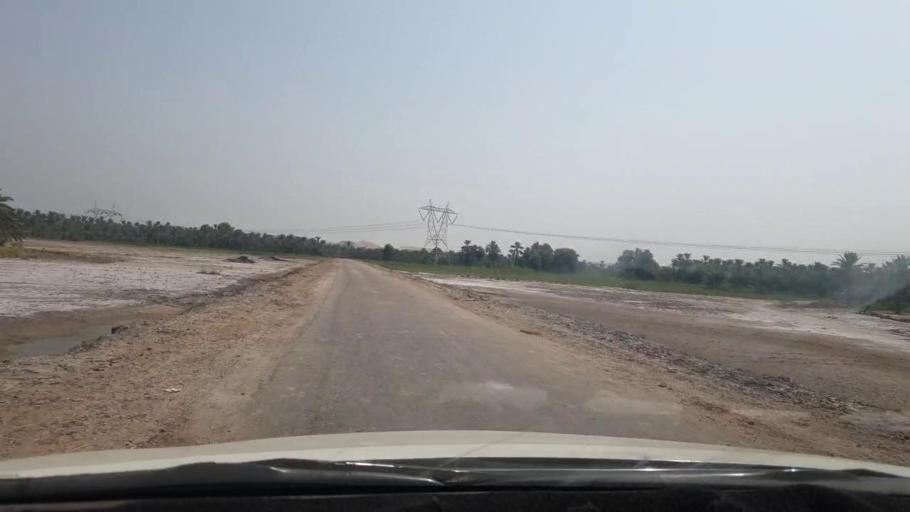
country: PK
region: Sindh
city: Rohri
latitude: 27.5968
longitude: 68.9029
